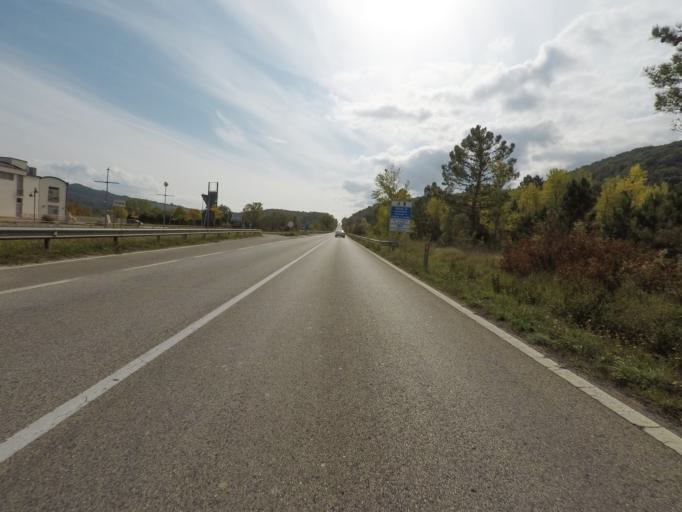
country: IT
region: Tuscany
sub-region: Provincia di Siena
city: Murlo
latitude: 43.1461
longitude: 11.2863
